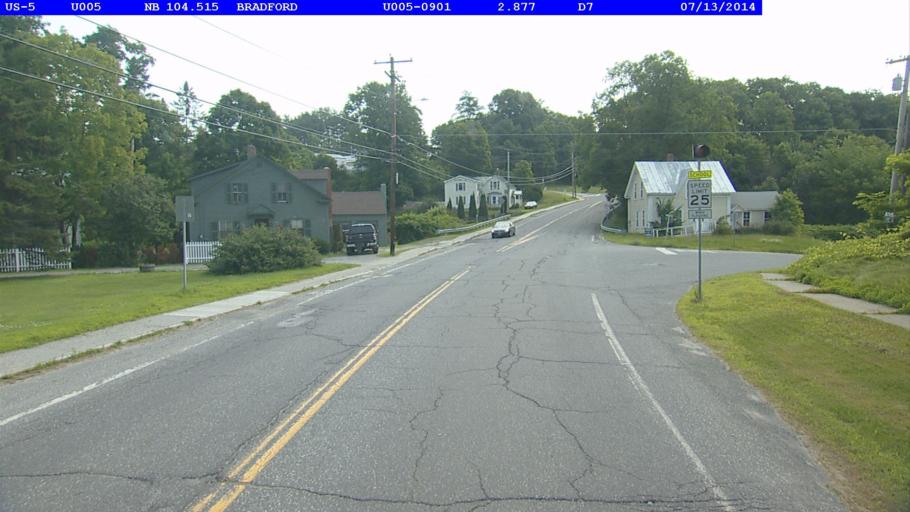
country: US
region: New Hampshire
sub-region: Grafton County
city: Haverhill
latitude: 44.0001
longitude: -72.1235
